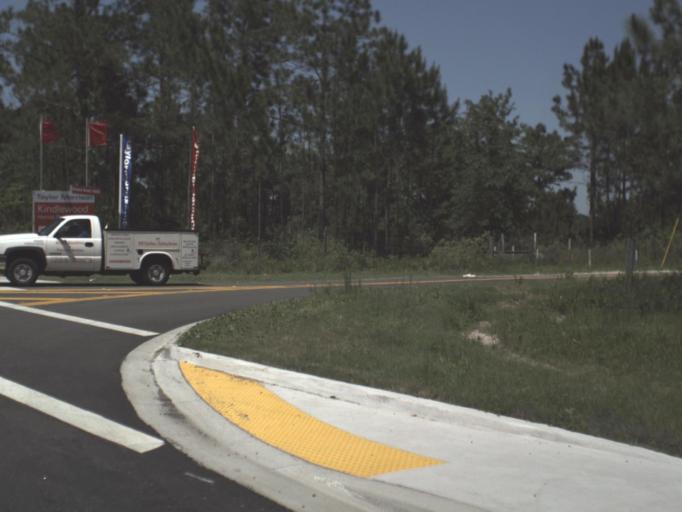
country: US
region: Florida
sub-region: Clay County
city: Lakeside
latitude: 30.1552
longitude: -81.8304
